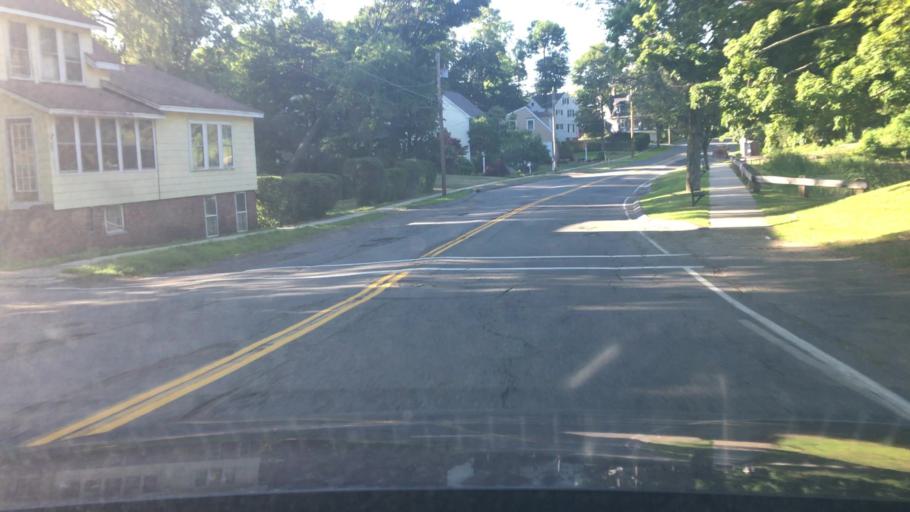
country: US
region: Massachusetts
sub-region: Essex County
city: Amesbury
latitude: 42.8543
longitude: -70.9383
